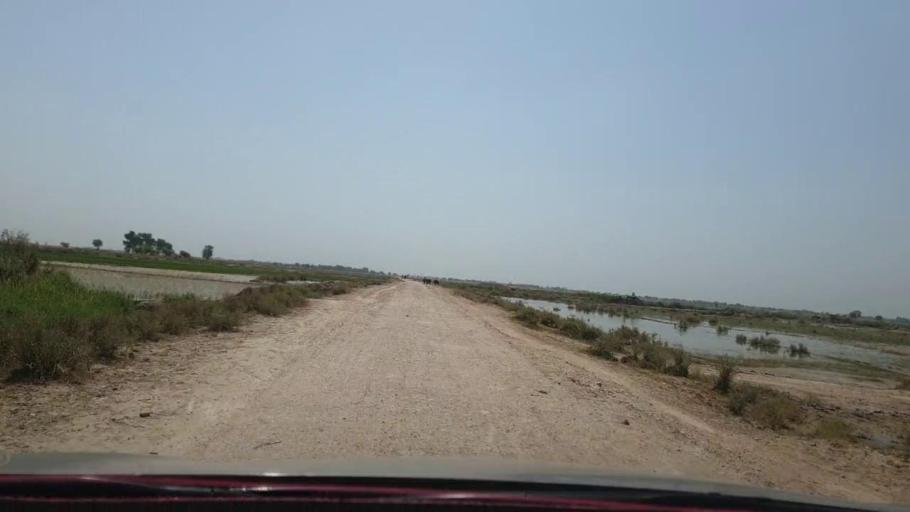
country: PK
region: Sindh
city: Kambar
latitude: 27.5834
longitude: 67.8768
